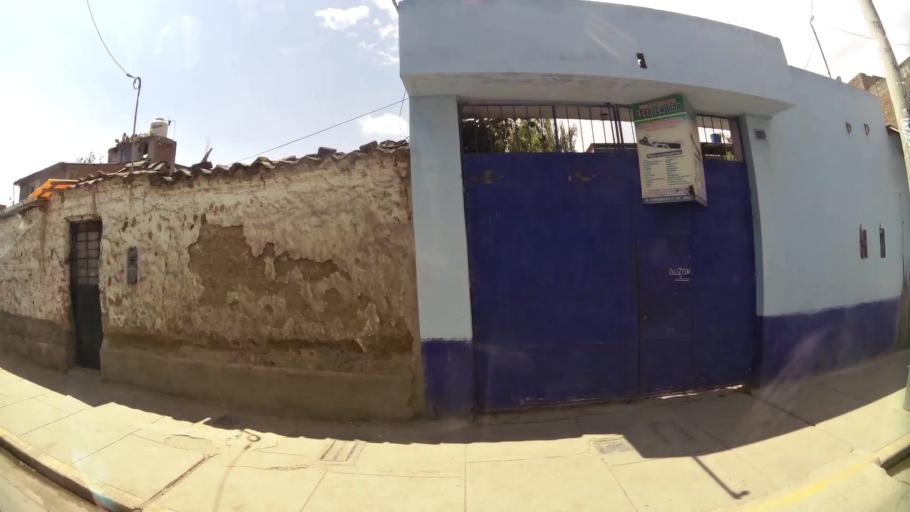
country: PE
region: Junin
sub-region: Provincia de Huancayo
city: El Tambo
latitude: -12.0795
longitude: -75.2091
